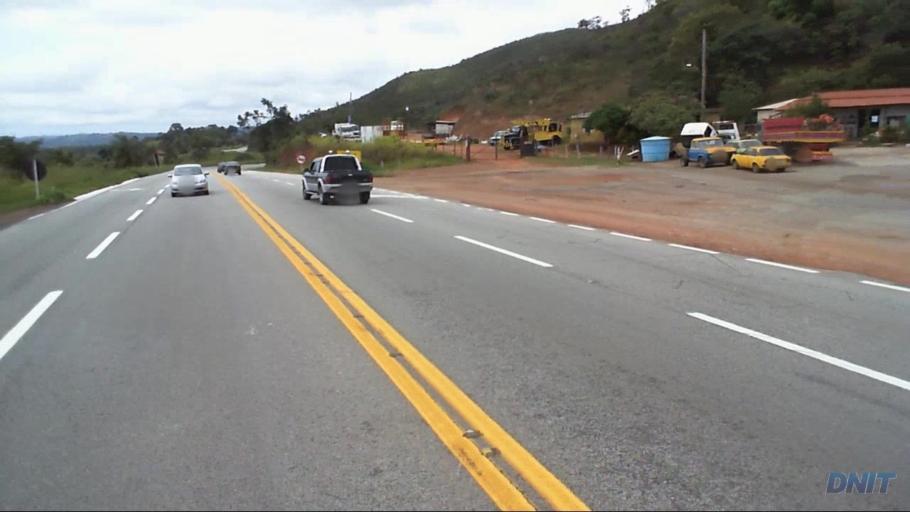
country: BR
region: Minas Gerais
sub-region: Caete
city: Caete
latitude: -19.7879
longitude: -43.6937
